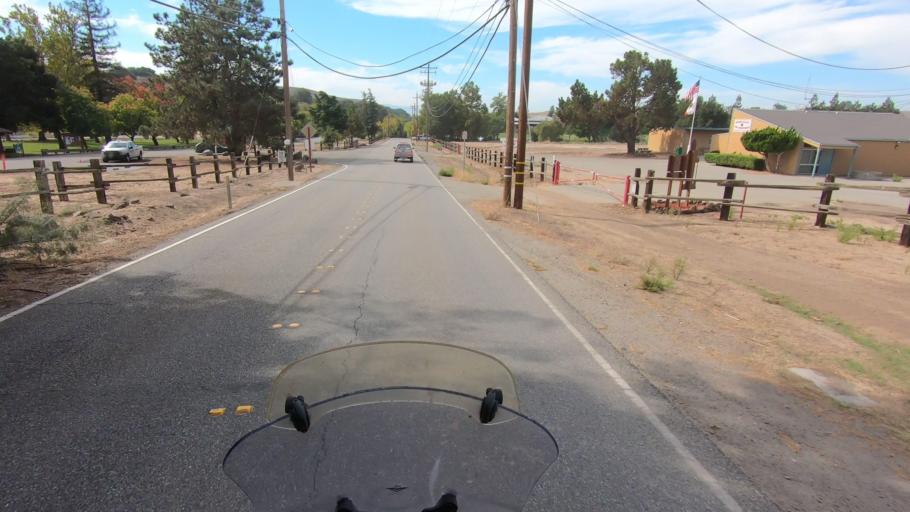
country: US
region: California
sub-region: Santa Clara County
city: Milpitas
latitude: 37.4483
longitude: -121.8482
